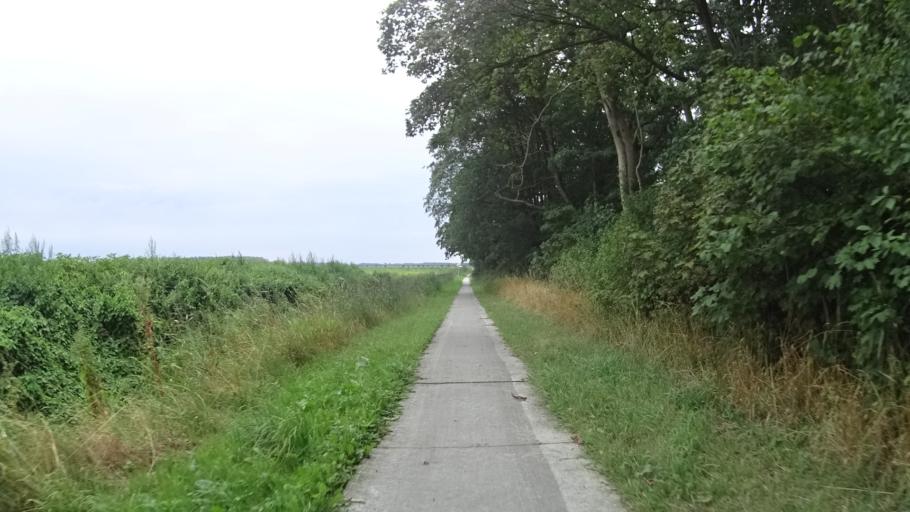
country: NL
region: Groningen
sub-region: Gemeente Slochteren
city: Slochteren
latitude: 53.2112
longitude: 6.8242
